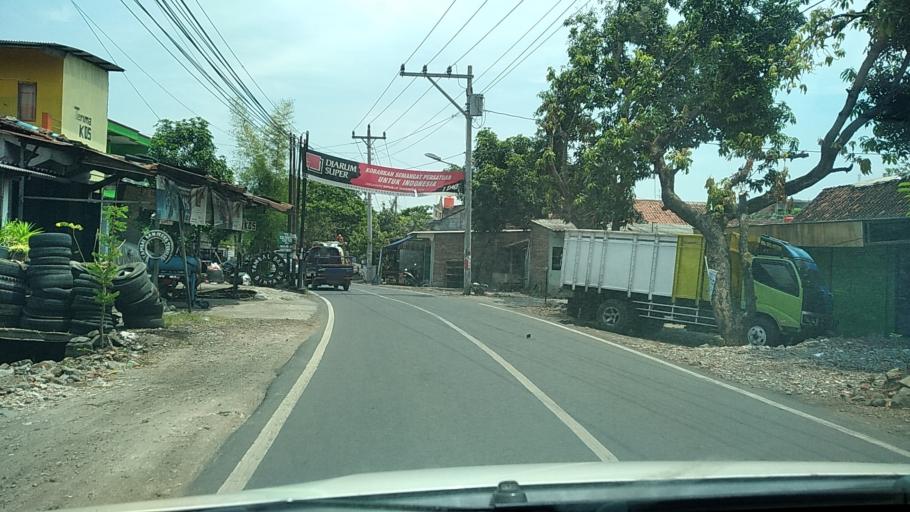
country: ID
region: Central Java
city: Mranggen
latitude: -7.0375
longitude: 110.4682
